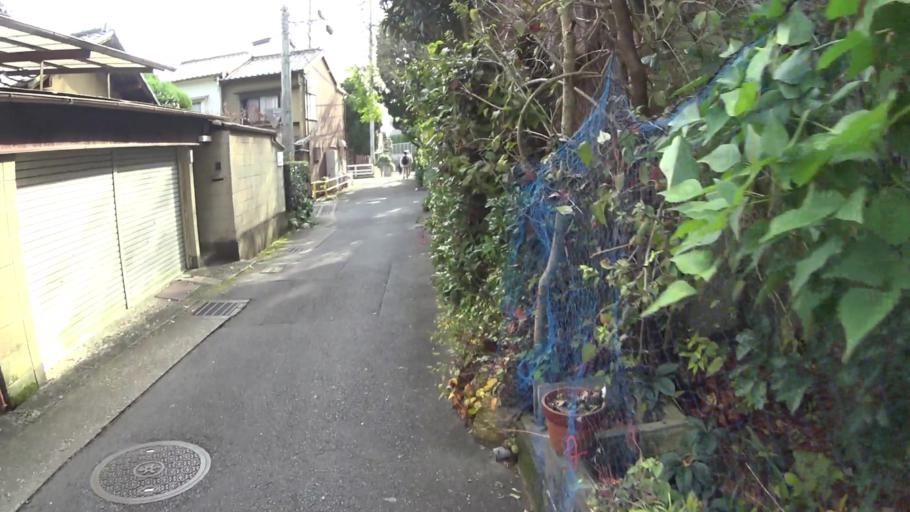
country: JP
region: Kyoto
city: Kyoto
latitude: 34.9991
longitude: 135.8032
